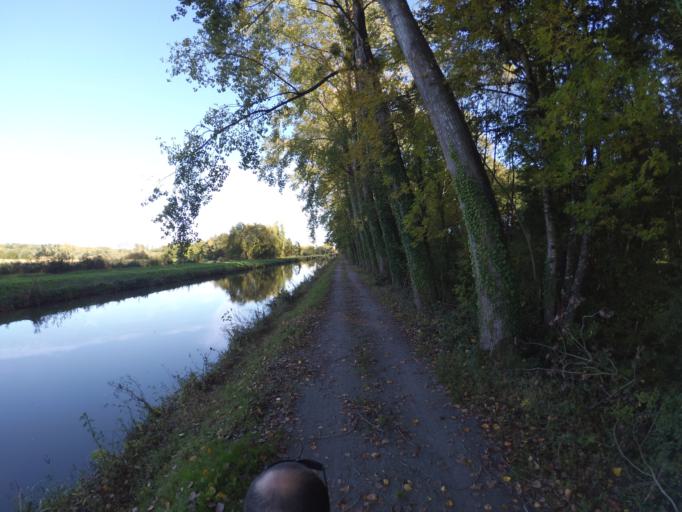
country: FR
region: Brittany
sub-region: Departement du Morbihan
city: Saint-Vincent-sur-Oust
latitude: 47.7185
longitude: -2.1563
